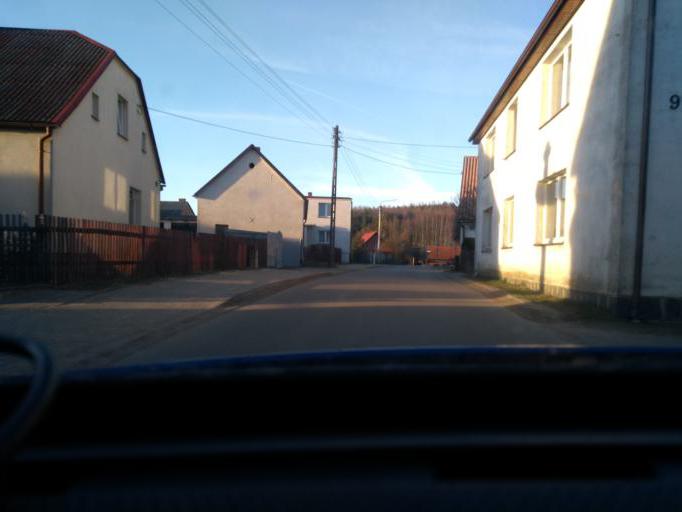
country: PL
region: Pomeranian Voivodeship
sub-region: Powiat kartuski
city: Przodkowo
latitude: 54.3767
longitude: 18.2642
